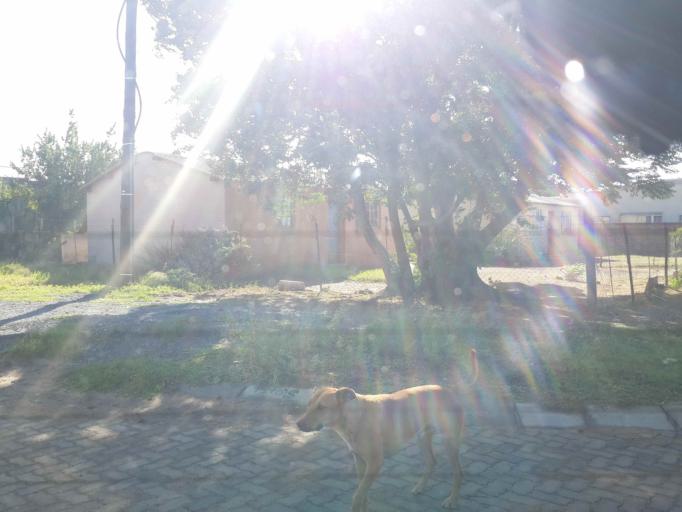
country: ZA
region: Northern Cape
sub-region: Siyanda District Municipality
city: Danielskuil
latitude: -28.1961
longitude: 23.5301
